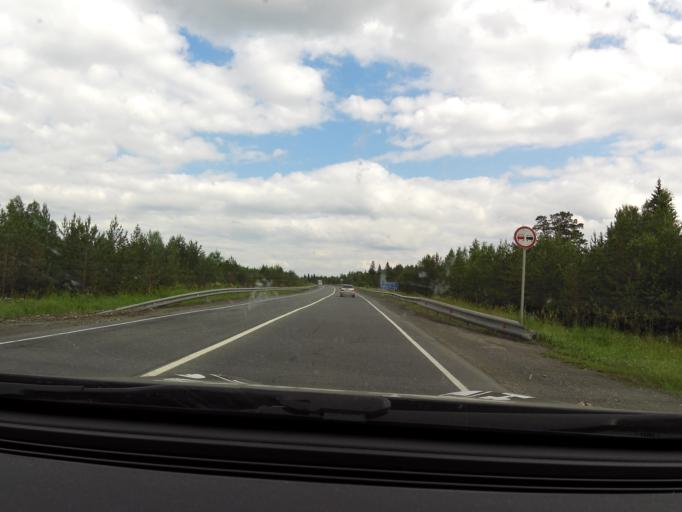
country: RU
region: Sverdlovsk
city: Atig
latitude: 56.7965
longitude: 59.3986
